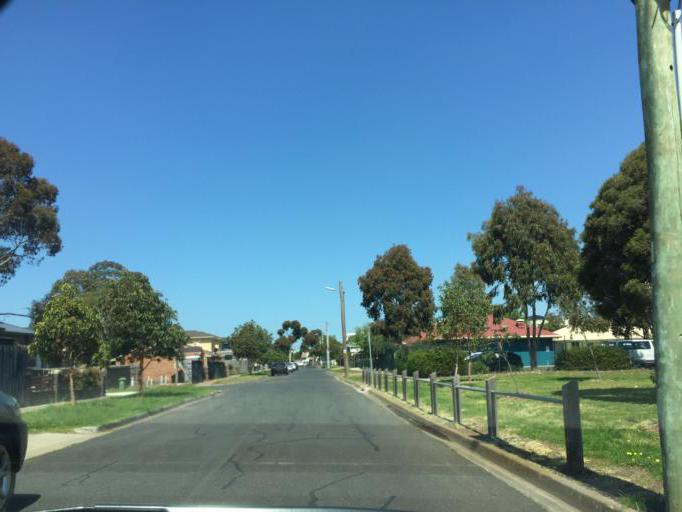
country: AU
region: Victoria
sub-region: Maribyrnong
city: Maidstone
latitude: -37.7876
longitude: 144.8743
